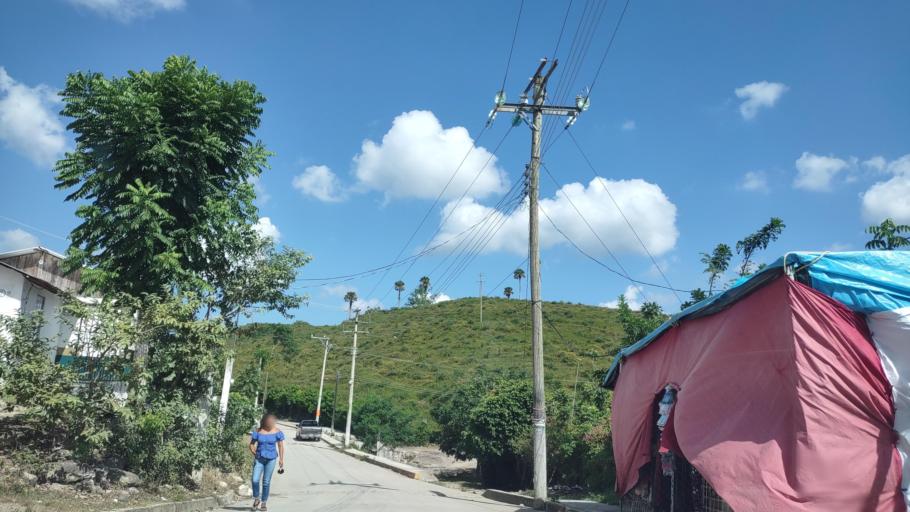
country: MM
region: Shan
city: Taunggyi
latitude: 20.5848
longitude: 97.3747
